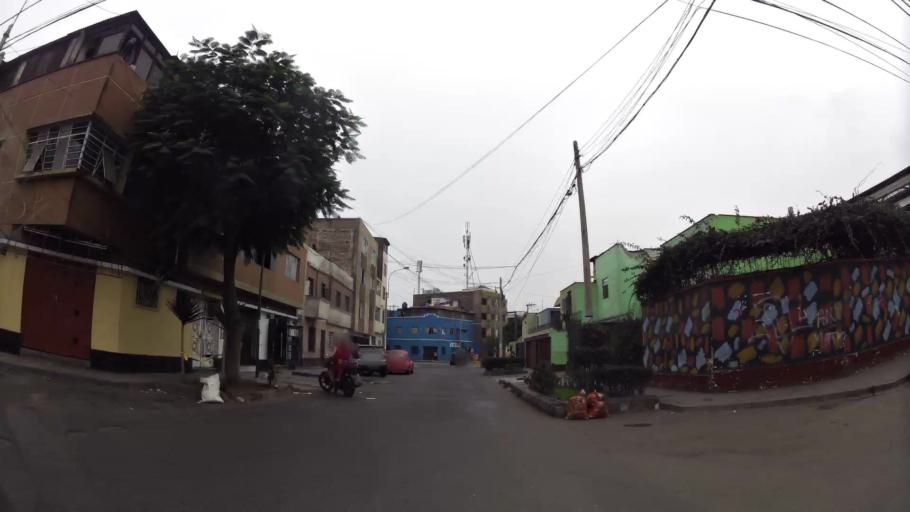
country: PE
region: Lima
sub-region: Lima
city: San Luis
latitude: -12.0764
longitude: -77.0240
